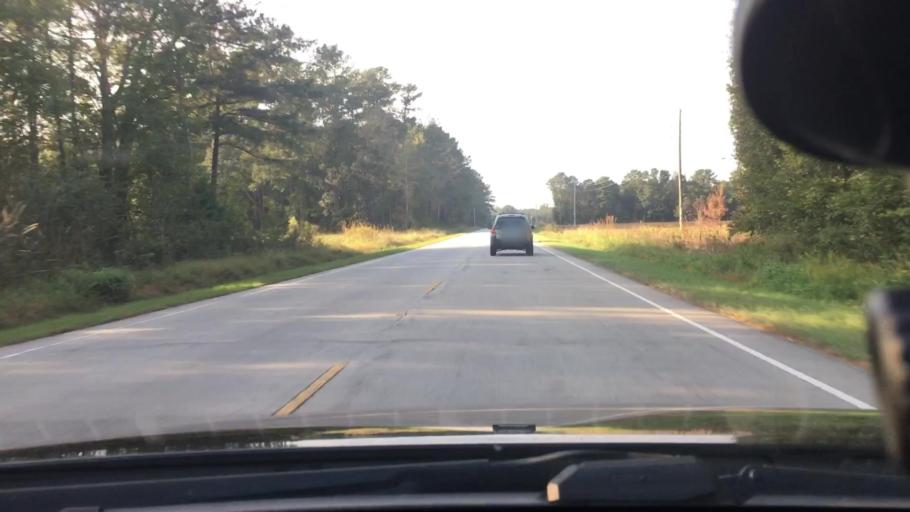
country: US
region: North Carolina
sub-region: Pitt County
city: Windsor
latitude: 35.4799
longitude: -77.2985
